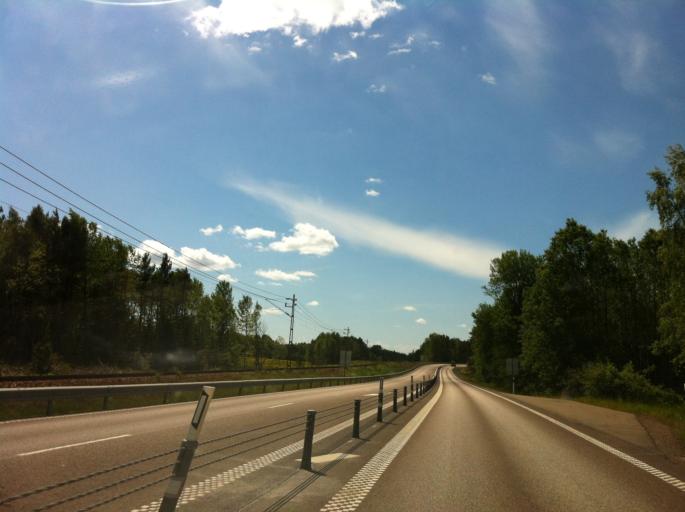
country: SE
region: Vaestra Goetaland
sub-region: Melleruds Kommun
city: Mellerud
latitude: 58.8629
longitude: 12.5602
